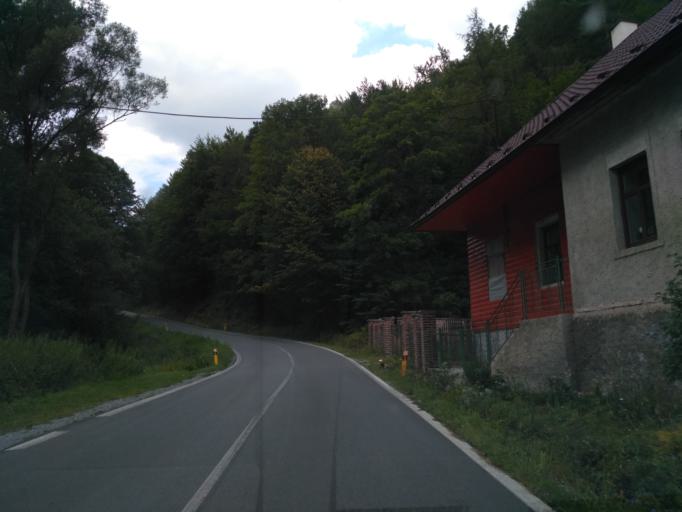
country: SK
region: Kosicky
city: Gelnica
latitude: 48.9095
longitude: 21.0298
